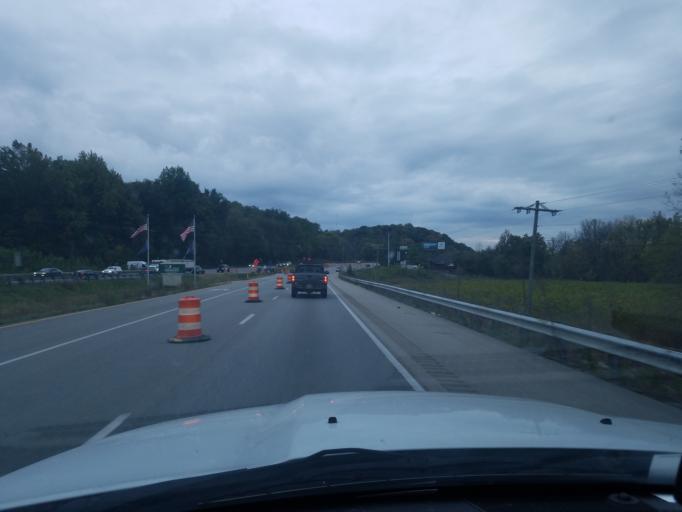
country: US
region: Kentucky
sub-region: Henderson County
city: Henderson
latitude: 37.8905
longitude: -87.5567
